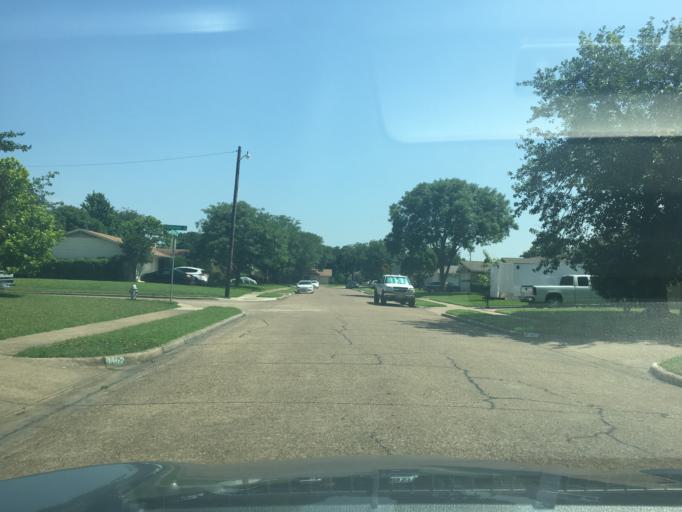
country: US
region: Texas
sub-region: Dallas County
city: Richardson
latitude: 32.9263
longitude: -96.7052
